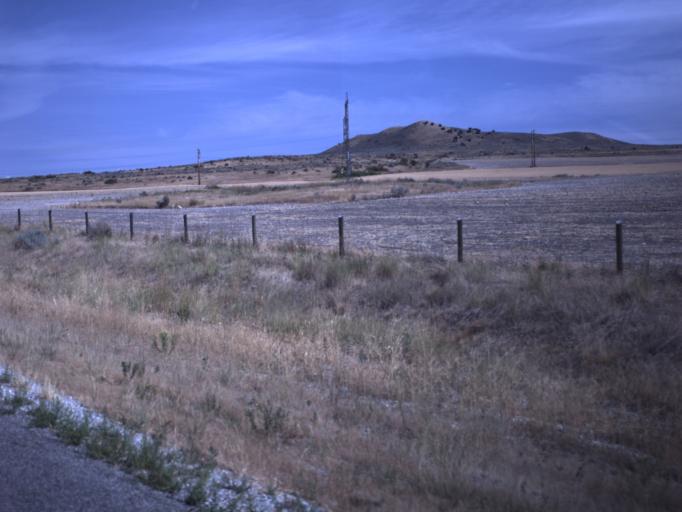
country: US
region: Utah
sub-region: Box Elder County
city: Garland
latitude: 41.7897
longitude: -112.0743
